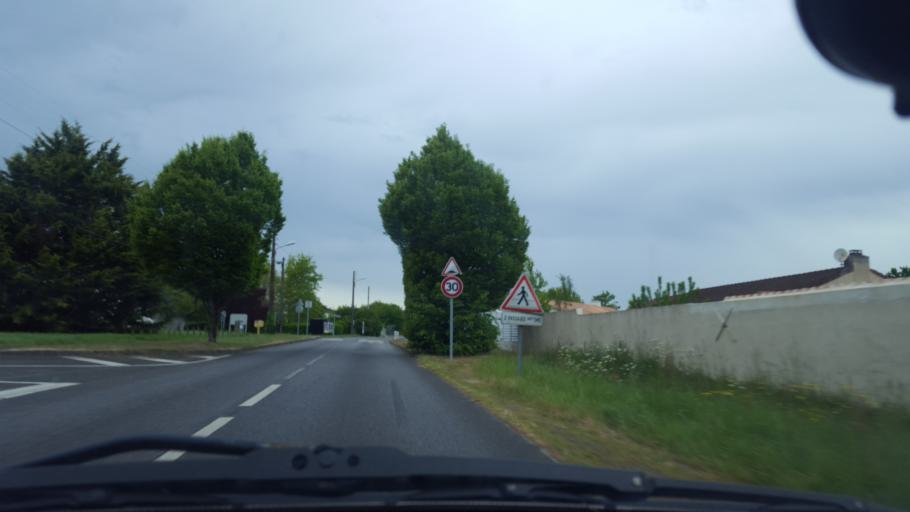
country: FR
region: Pays de la Loire
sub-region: Departement de la Loire-Atlantique
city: Les Sorinieres
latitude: 47.1586
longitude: -1.5161
